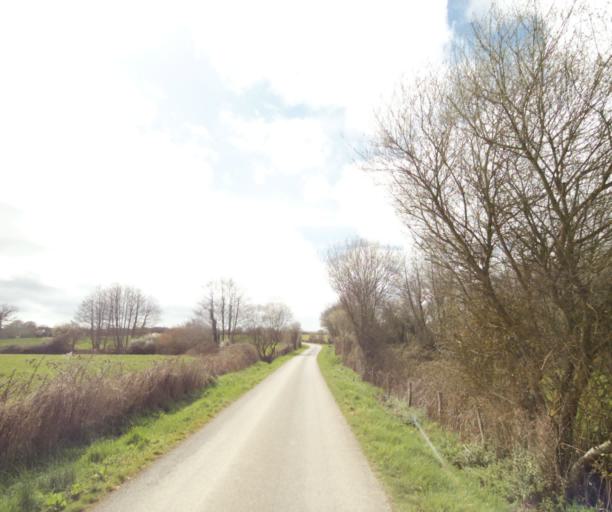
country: FR
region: Pays de la Loire
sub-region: Departement de la Loire-Atlantique
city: Bouvron
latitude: 47.4252
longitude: -1.8774
